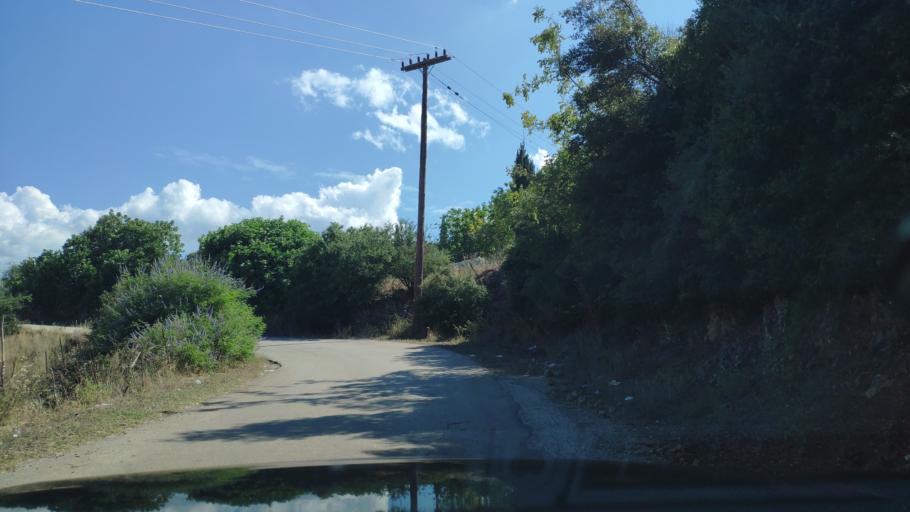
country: GR
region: West Greece
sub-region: Nomos Aitolias kai Akarnanias
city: Katouna
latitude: 38.7924
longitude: 21.1149
